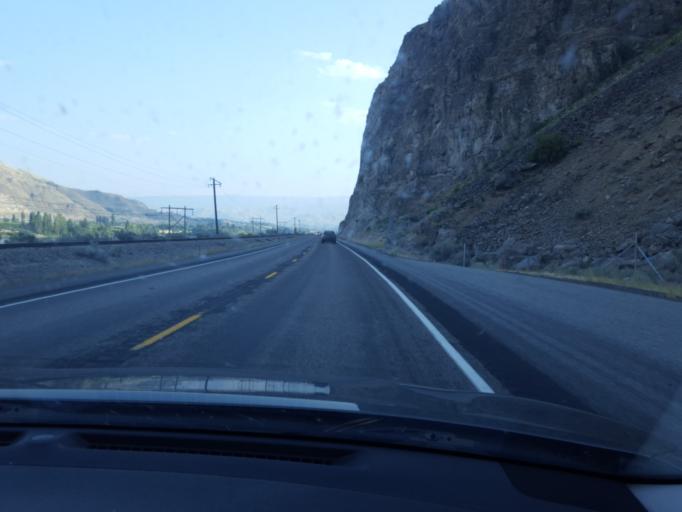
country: US
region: Washington
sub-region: Chelan County
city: Sunnyslope
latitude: 47.5195
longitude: -120.3072
